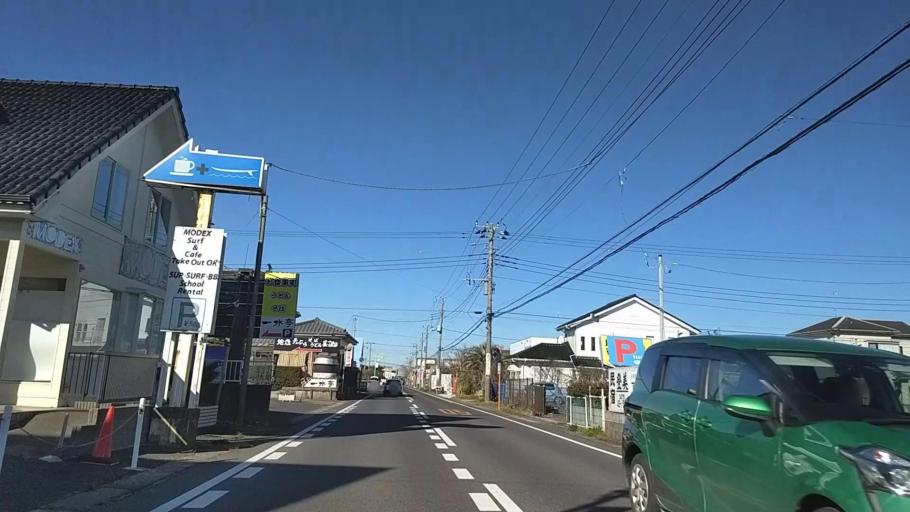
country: JP
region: Chiba
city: Ohara
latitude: 35.3560
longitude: 140.3888
